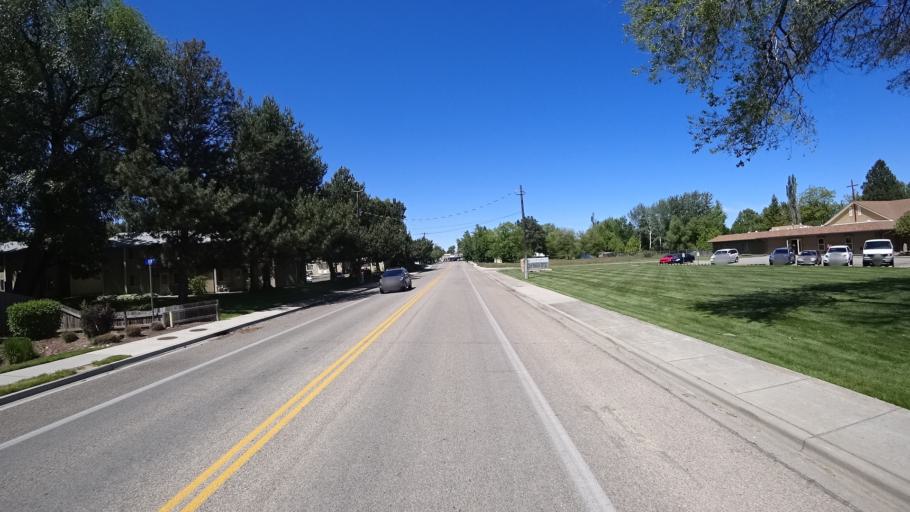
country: US
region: Idaho
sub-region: Ada County
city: Boise
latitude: 43.5862
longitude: -116.1803
